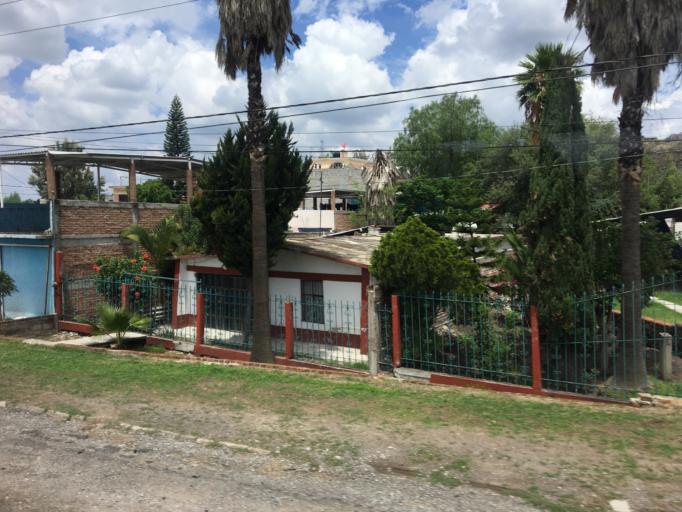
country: MX
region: Guanajuato
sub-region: Irapuato
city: Ex-Hacienda del Copal
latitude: 20.7307
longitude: -101.3432
